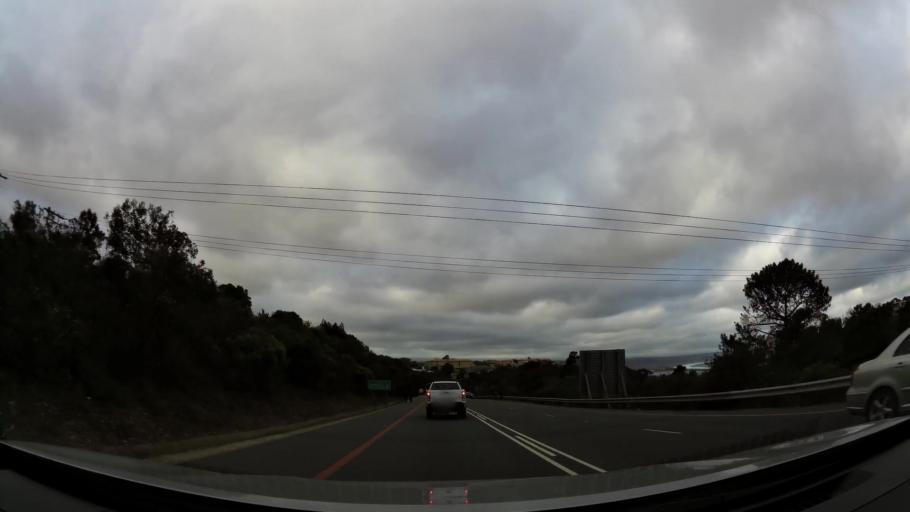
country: ZA
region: Western Cape
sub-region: Eden District Municipality
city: Plettenberg Bay
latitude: -34.0470
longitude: 23.3611
